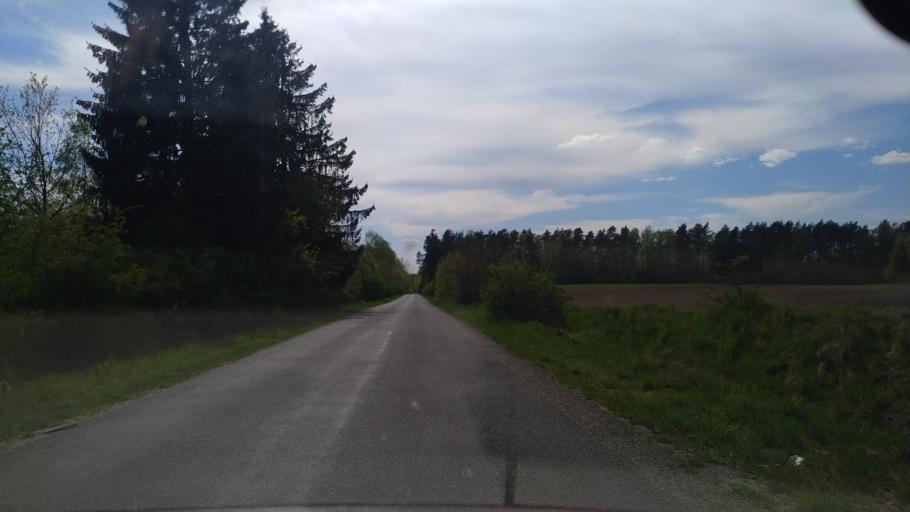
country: PL
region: West Pomeranian Voivodeship
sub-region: Powiat walecki
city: Miroslawiec
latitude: 53.3504
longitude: 16.2722
